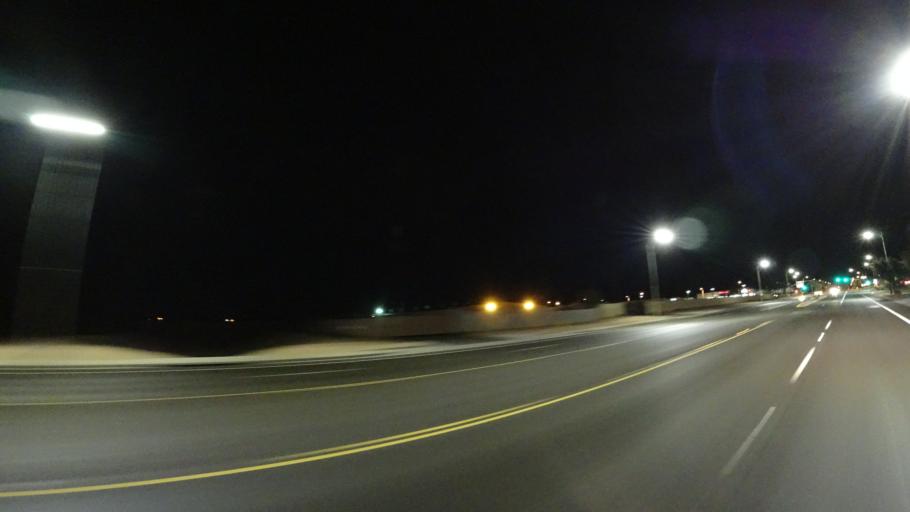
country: US
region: Arizona
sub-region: Maricopa County
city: Sun Lakes
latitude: 33.2210
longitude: -111.8240
